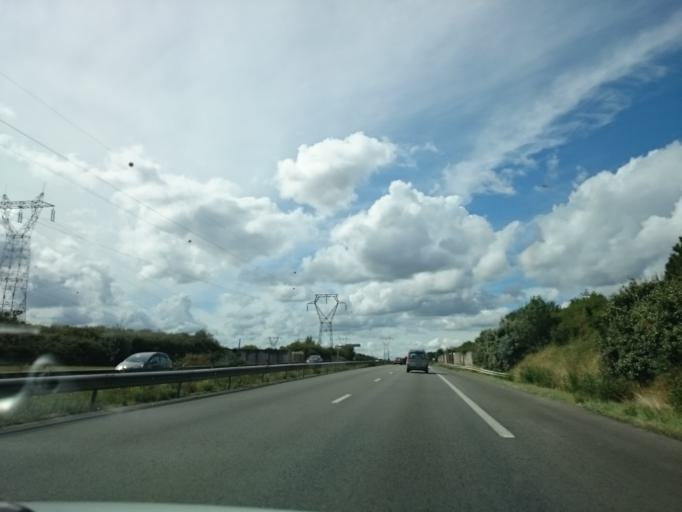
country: FR
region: Pays de la Loire
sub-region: Departement de la Loire-Atlantique
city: Reze
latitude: 47.1660
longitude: -1.5713
